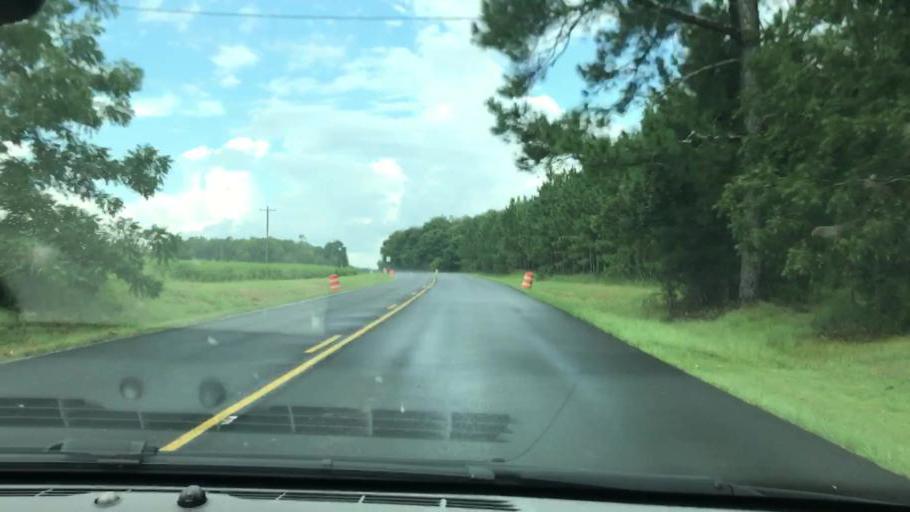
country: US
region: Georgia
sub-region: Early County
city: Blakely
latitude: 31.4328
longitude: -84.9730
